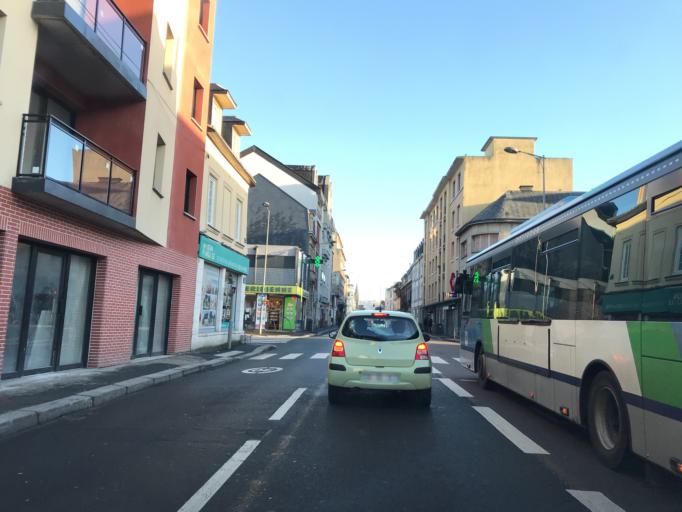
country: FR
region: Haute-Normandie
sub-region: Departement de la Seine-Maritime
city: Sotteville-les-Rouen
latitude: 49.4254
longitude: 1.0824
